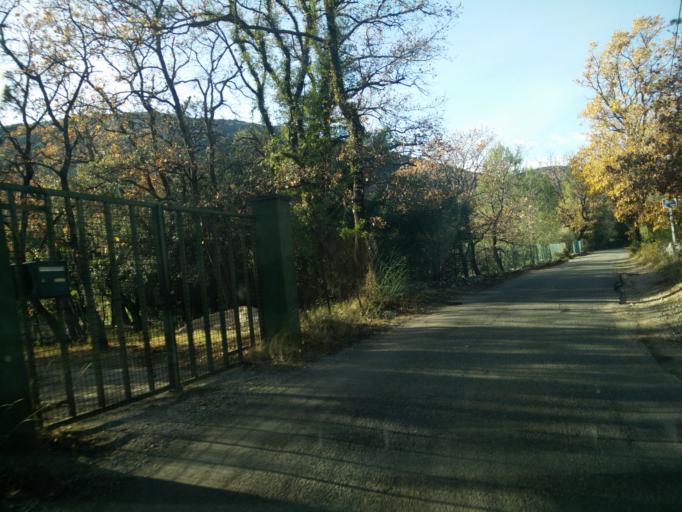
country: FR
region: Provence-Alpes-Cote d'Azur
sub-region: Departement du Var
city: Sollies-Toucas
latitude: 43.2028
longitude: 5.9885
